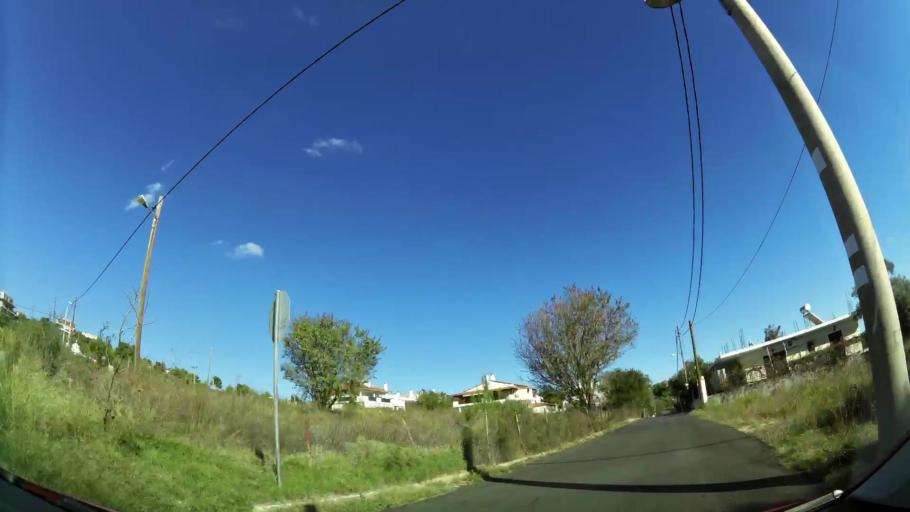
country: GR
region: Attica
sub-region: Nomarchia Anatolikis Attikis
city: Anthousa
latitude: 38.0186
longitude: 23.8728
